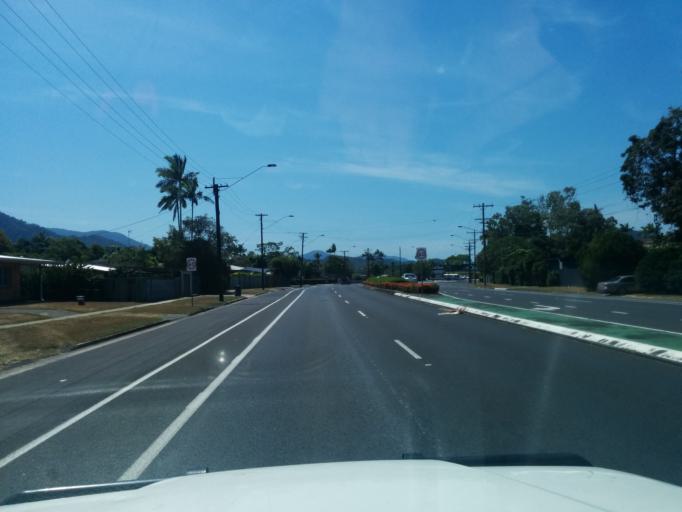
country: AU
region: Queensland
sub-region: Cairns
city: Woree
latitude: -16.9353
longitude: 145.7440
